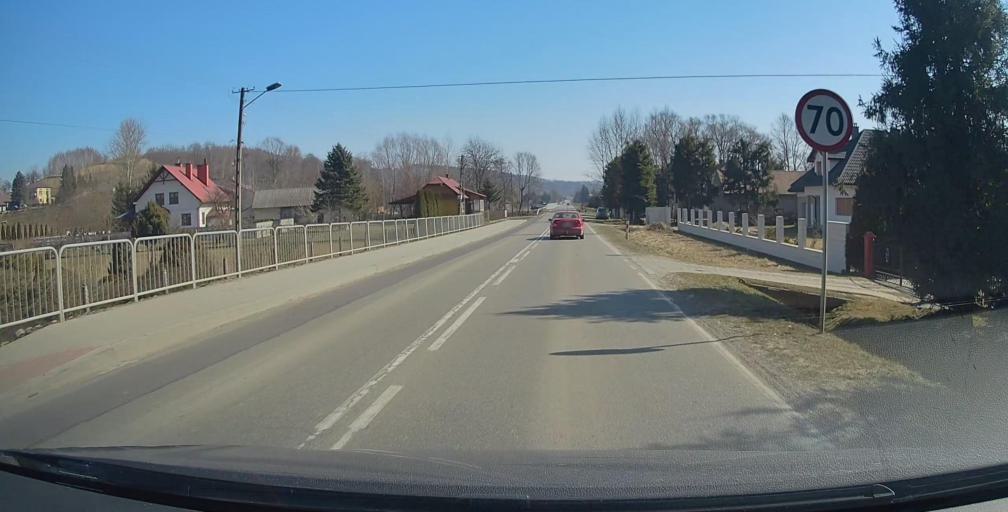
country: PL
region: Subcarpathian Voivodeship
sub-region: Powiat rzeszowski
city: Tyczyn
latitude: 49.9657
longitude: 22.0763
